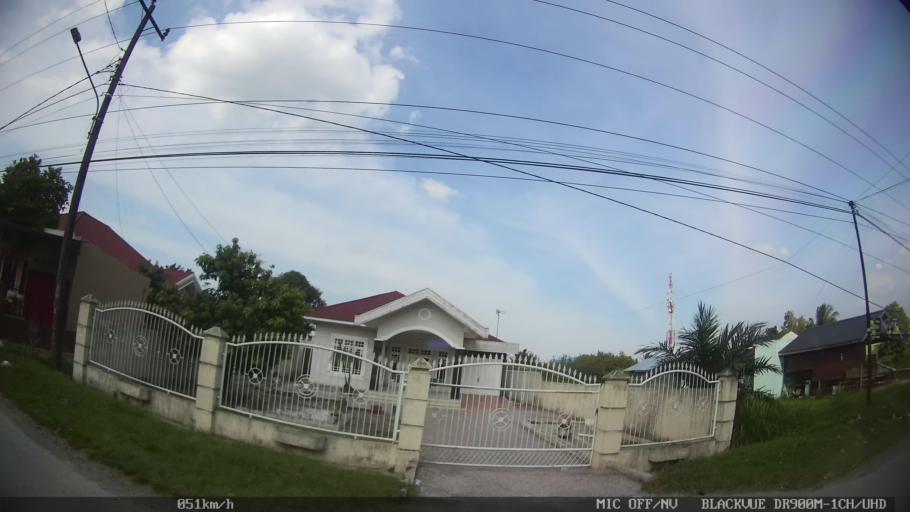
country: ID
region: North Sumatra
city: Binjai
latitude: 3.6333
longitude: 98.4898
